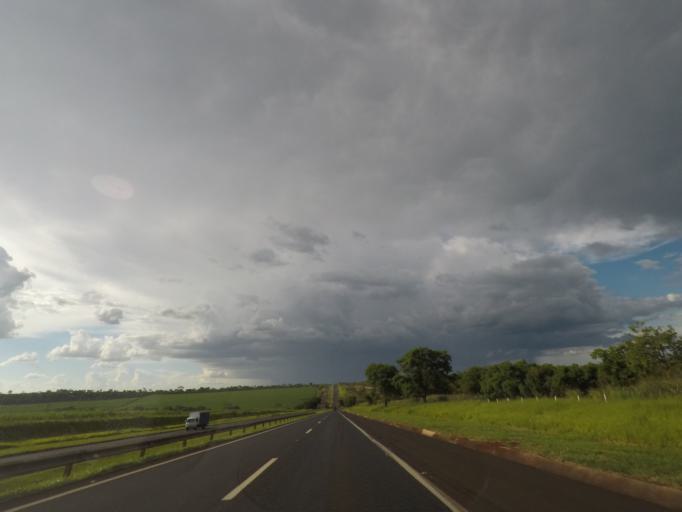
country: BR
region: Sao Paulo
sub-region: Jardinopolis
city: Jardinopolis
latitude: -21.0142
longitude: -47.8433
